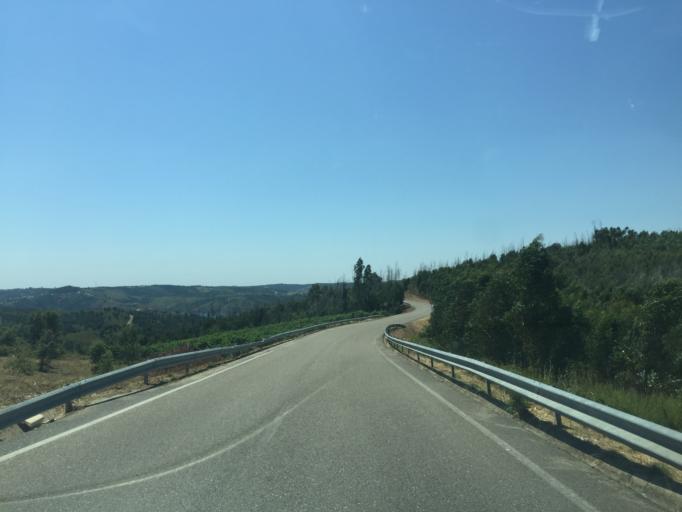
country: PT
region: Santarem
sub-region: Ferreira do Zezere
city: Ferreira do Zezere
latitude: 39.5849
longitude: -8.2969
